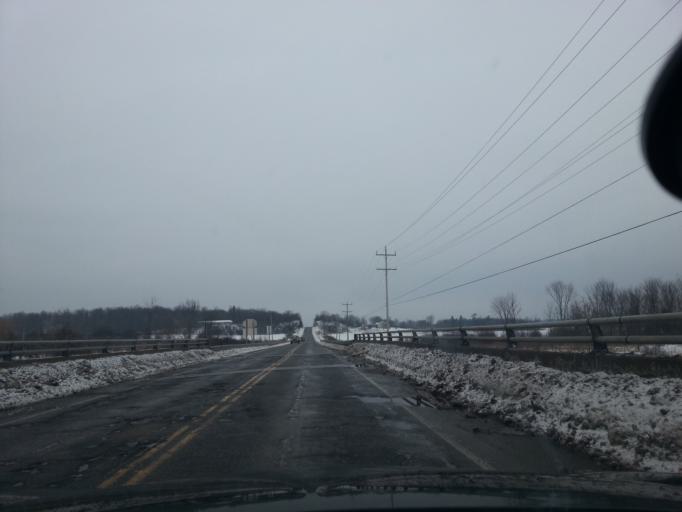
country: CA
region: Ontario
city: Arnprior
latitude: 45.3947
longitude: -76.1838
